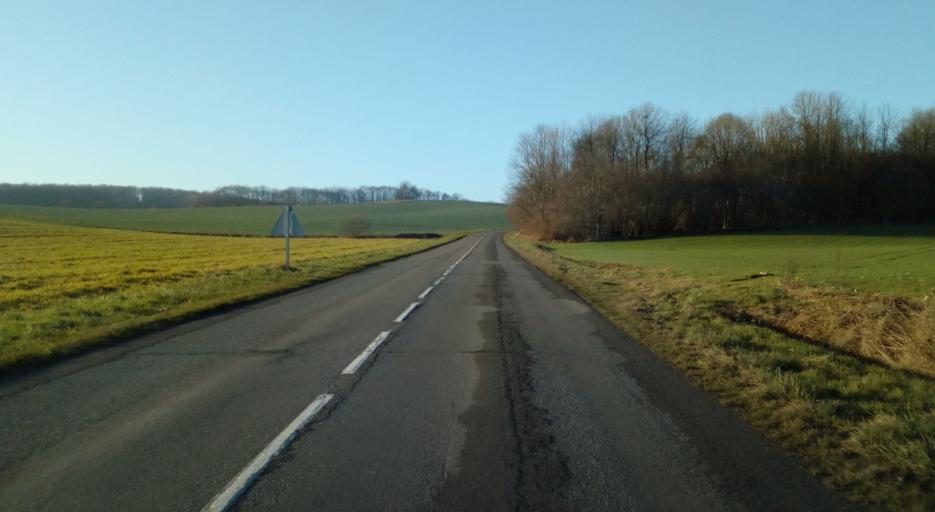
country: FR
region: Champagne-Ardenne
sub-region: Departement des Ardennes
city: Signy-le-Petit
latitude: 49.7781
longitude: 4.3797
